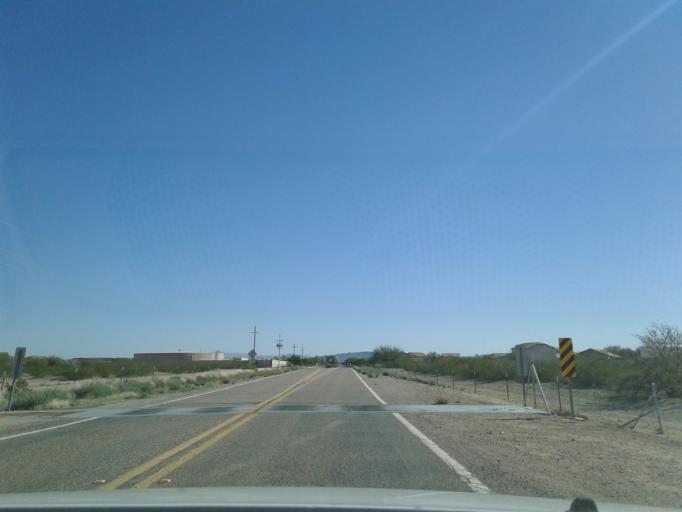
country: US
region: Arizona
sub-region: Pima County
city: Avra Valley
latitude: 32.5661
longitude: -111.3483
